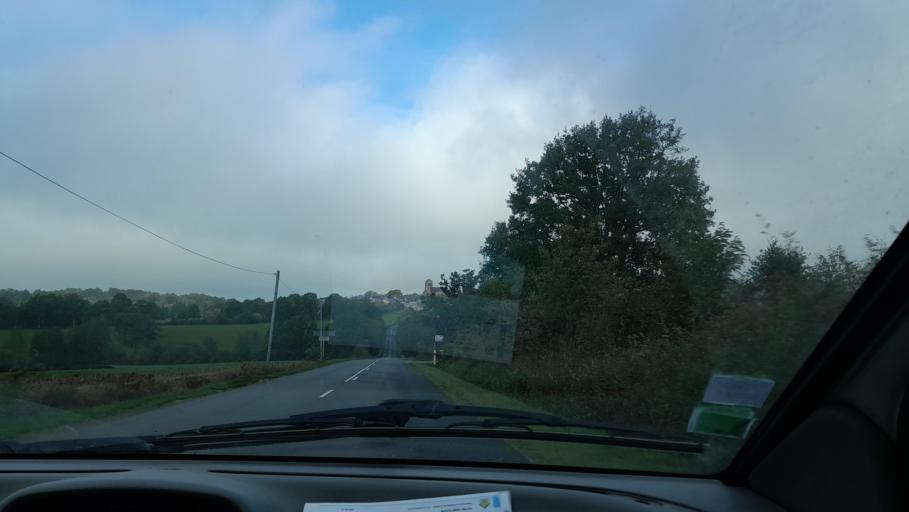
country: FR
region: Pays de la Loire
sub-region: Departement de la Mayenne
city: Juvigne
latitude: 48.2132
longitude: -1.0796
